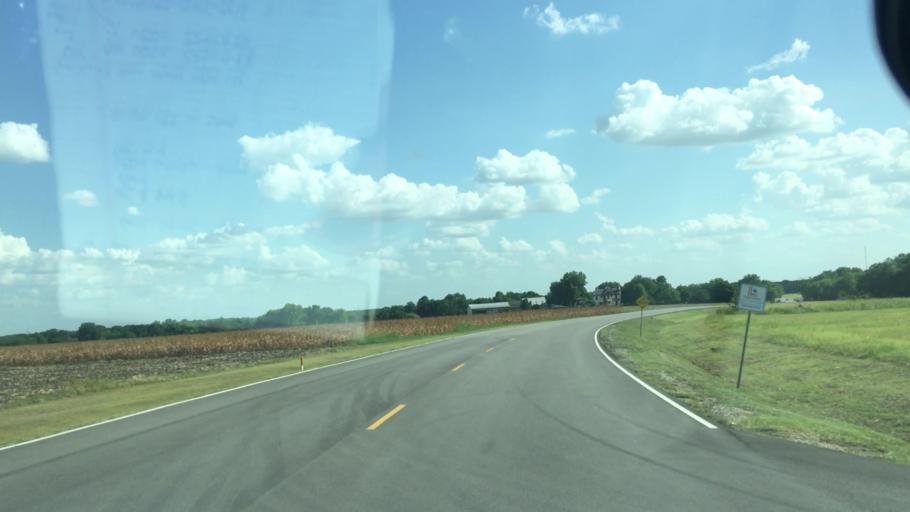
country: US
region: Texas
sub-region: Dallas County
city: Lancaster
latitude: 32.5922
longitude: -96.7482
